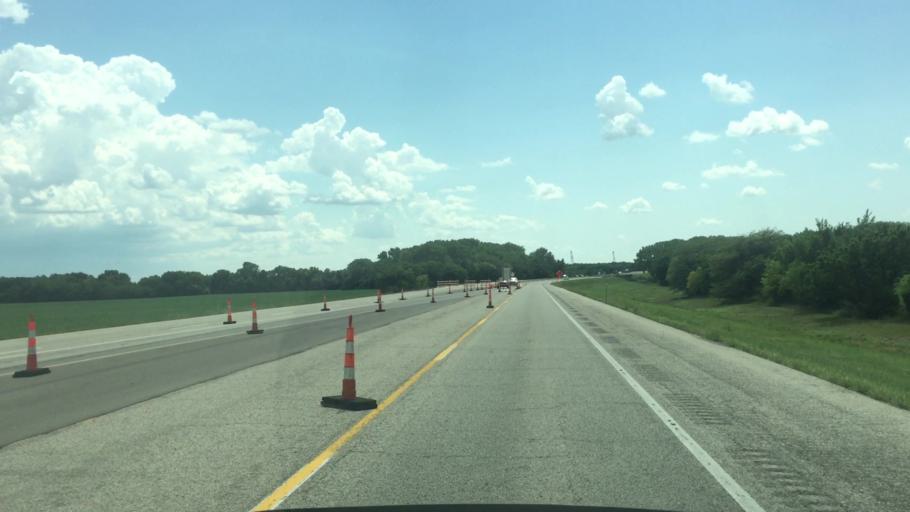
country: US
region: Kansas
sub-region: Lyon County
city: Emporia
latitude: 38.4588
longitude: -96.1946
